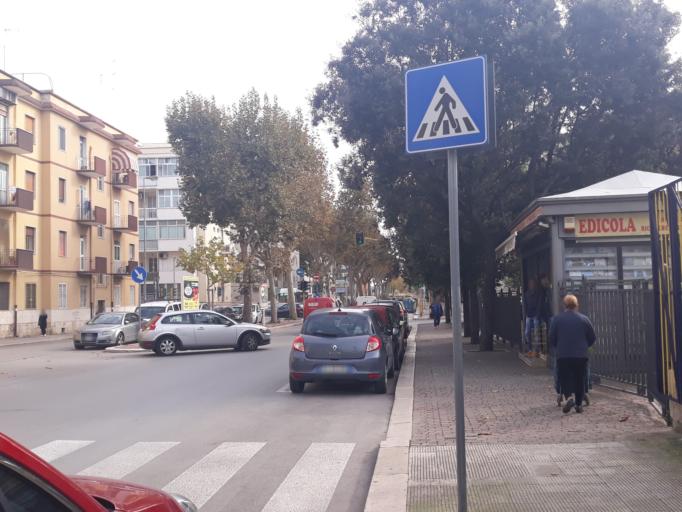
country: IT
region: Apulia
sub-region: Provincia di Bari
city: Bari
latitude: 41.1141
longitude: 16.8899
